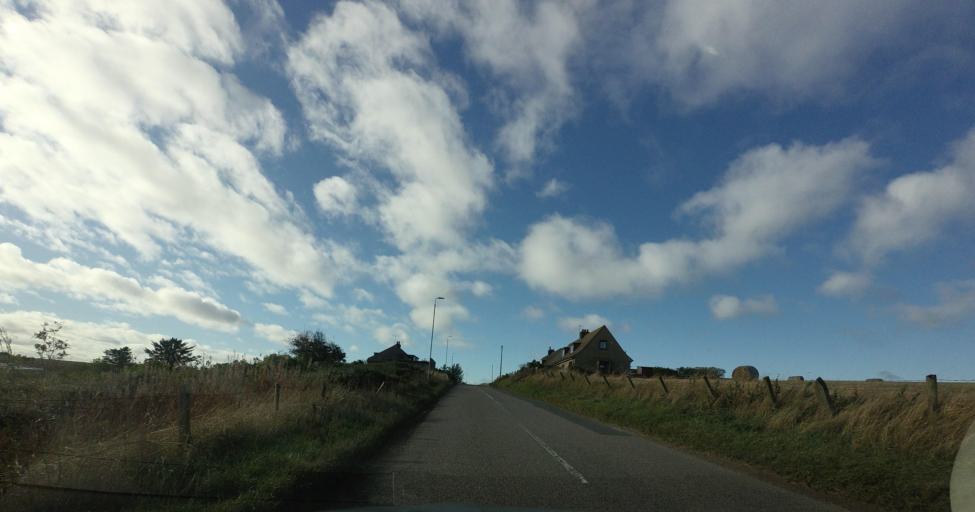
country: GB
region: Scotland
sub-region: Aberdeenshire
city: Macduff
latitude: 57.6638
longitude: -2.4525
